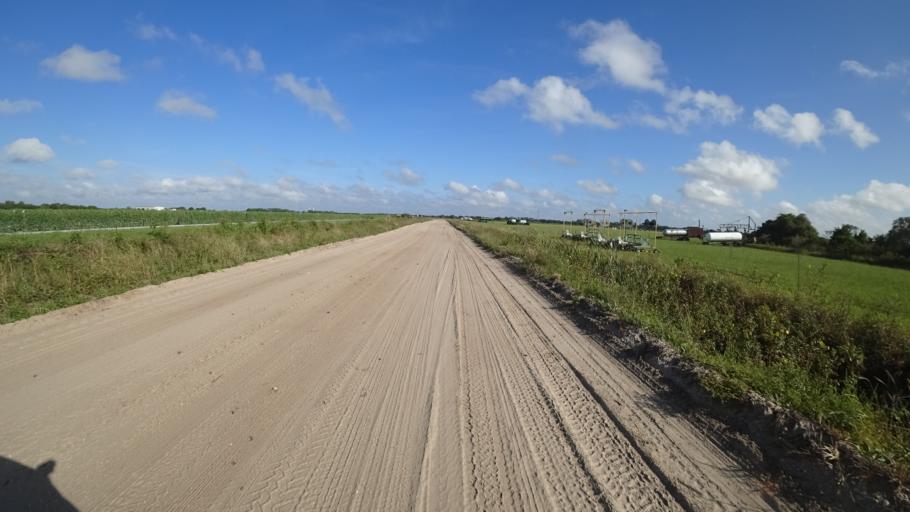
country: US
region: Florida
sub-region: Hillsborough County
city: Wimauma
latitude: 27.5391
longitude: -82.3179
